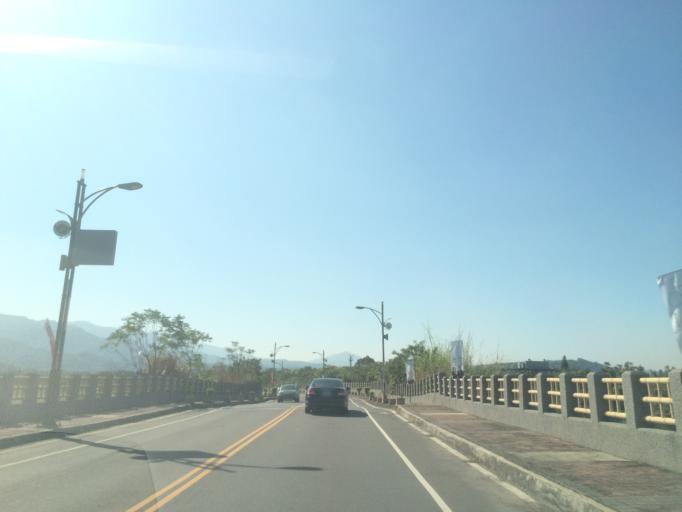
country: TW
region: Taiwan
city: Lugu
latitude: 23.7879
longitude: 120.7054
